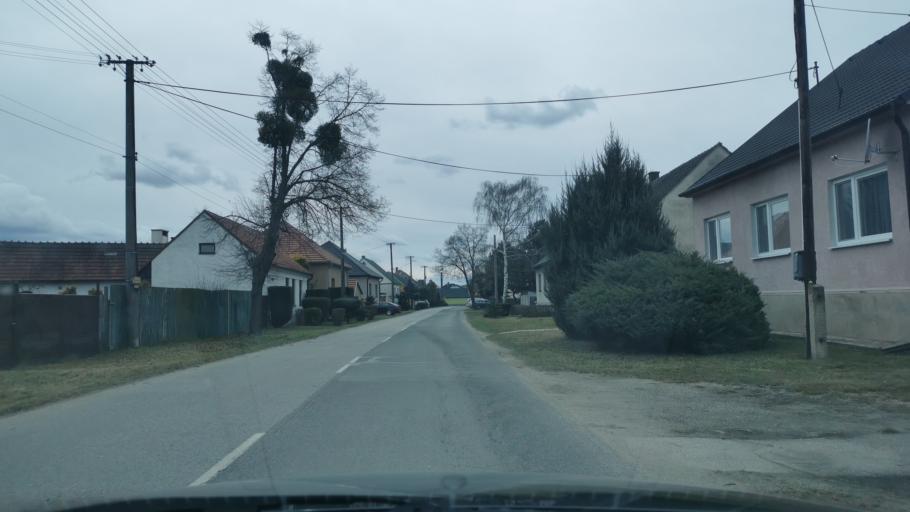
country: CZ
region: South Moravian
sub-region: Okres Breclav
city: Lanzhot
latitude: 48.6941
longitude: 17.0157
